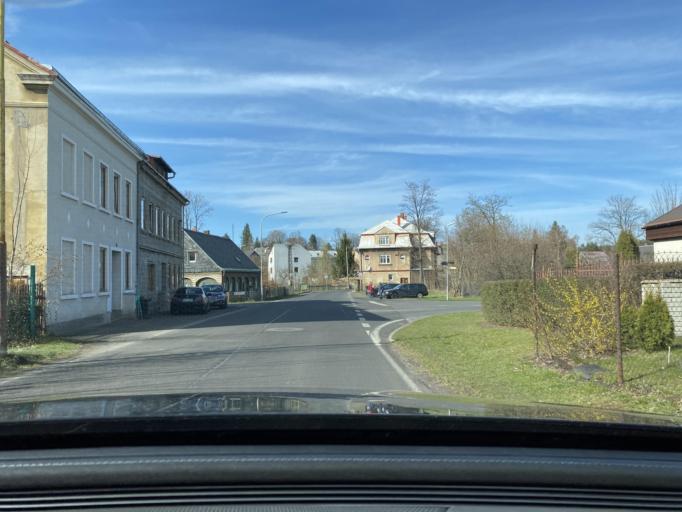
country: CZ
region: Ustecky
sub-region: Okres Decin
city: Sluknov
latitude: 51.0050
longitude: 14.4527
